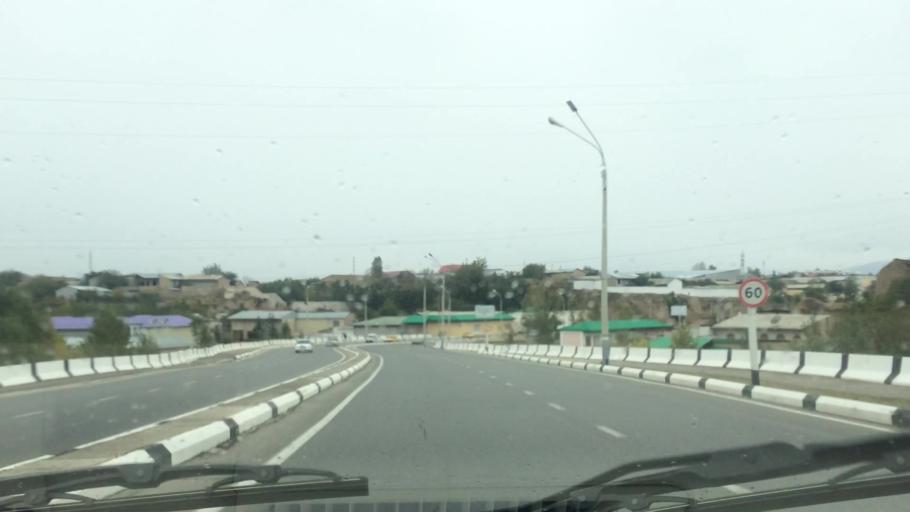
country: UZ
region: Samarqand
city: Samarqand
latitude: 39.6724
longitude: 66.9999
